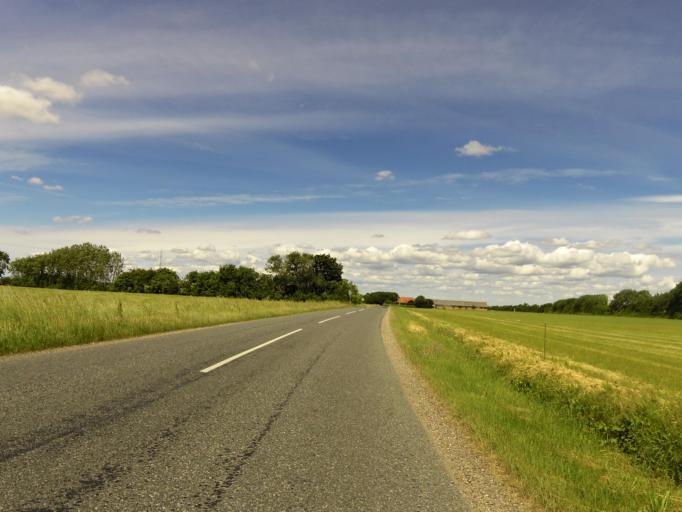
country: DK
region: South Denmark
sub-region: Esbjerg Kommune
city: Ribe
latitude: 55.2669
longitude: 8.8079
